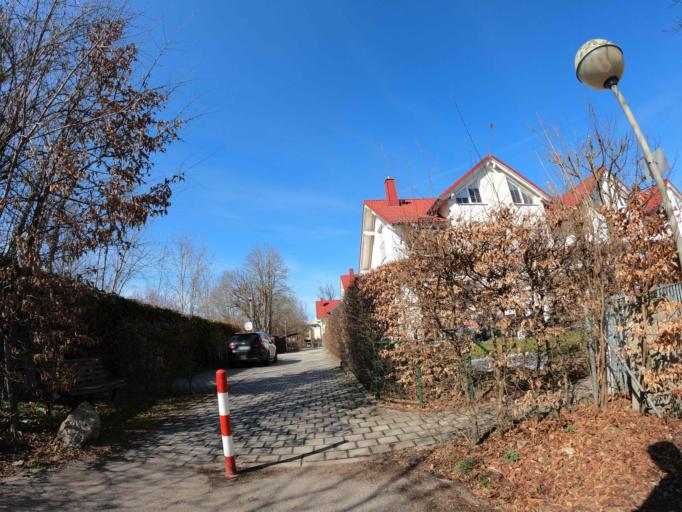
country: DE
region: Bavaria
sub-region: Upper Bavaria
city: Taufkirchen
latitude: 48.0487
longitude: 11.6170
